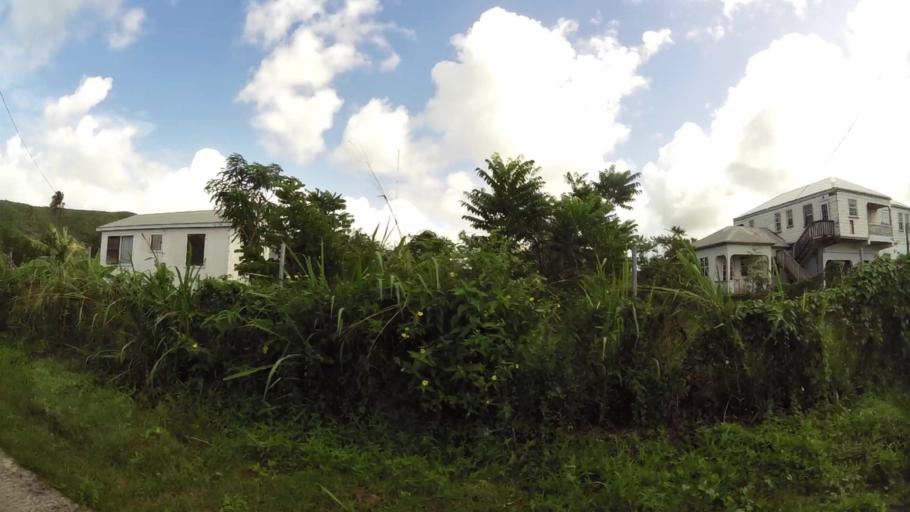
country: AG
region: Saint Mary
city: Bolands
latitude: 17.0759
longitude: -61.8753
